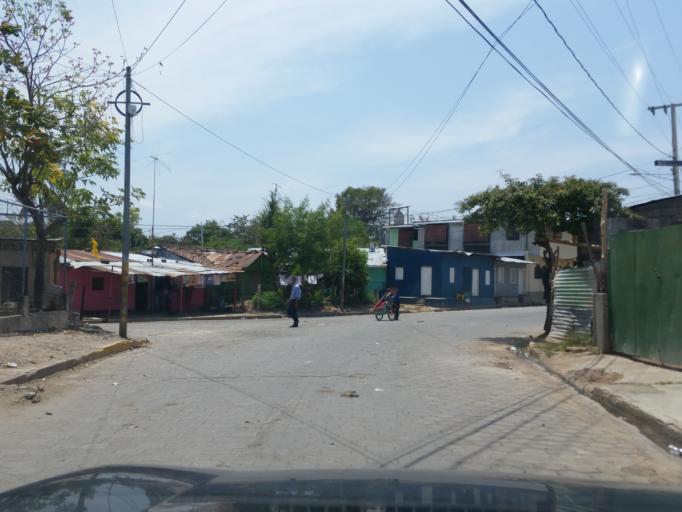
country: NI
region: Granada
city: Granada
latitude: 11.9276
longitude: -85.9483
